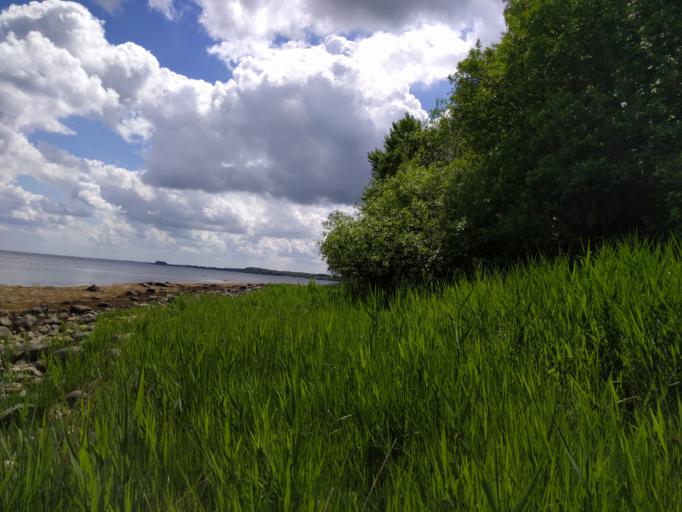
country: DK
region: South Denmark
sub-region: Aabenraa Kommune
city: Lojt Kirkeby
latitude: 55.1288
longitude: 9.5200
